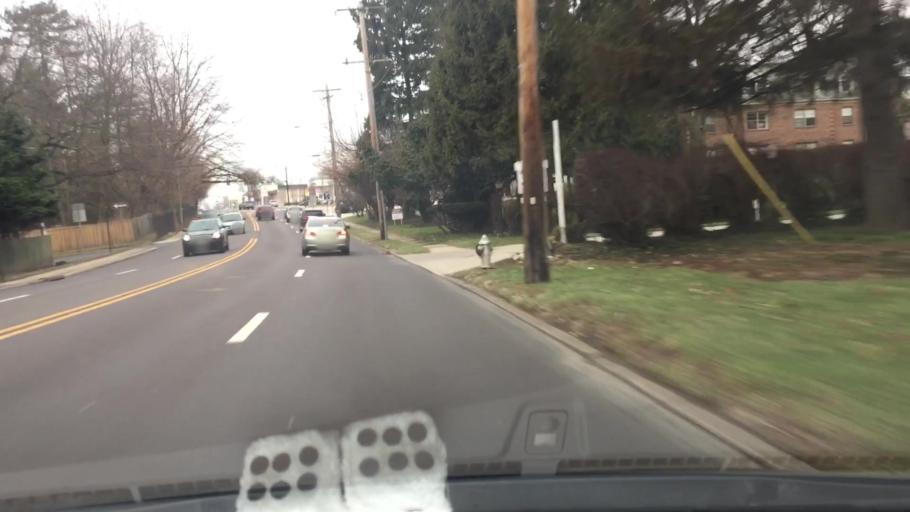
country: US
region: Pennsylvania
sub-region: Montgomery County
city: Ardmore
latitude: 40.0005
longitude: -75.2744
